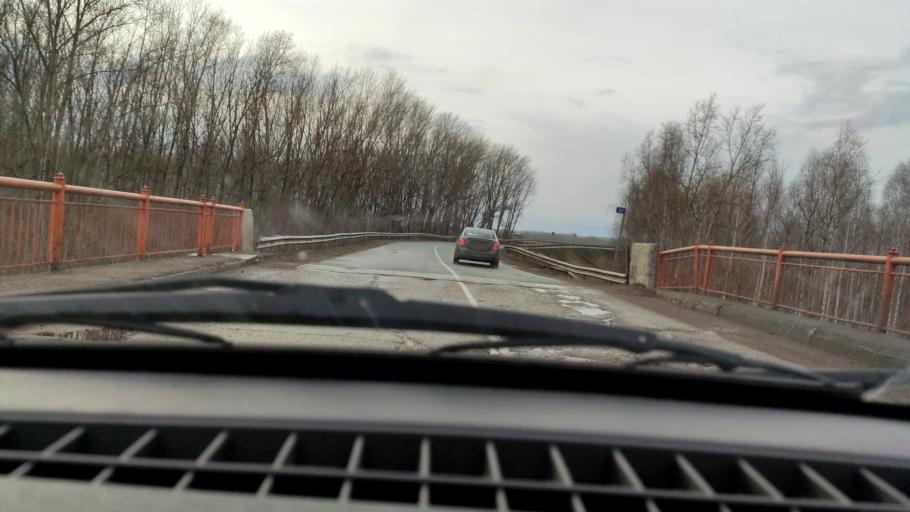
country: RU
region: Bashkortostan
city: Alekseyevka
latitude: 55.0787
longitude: 55.0690
